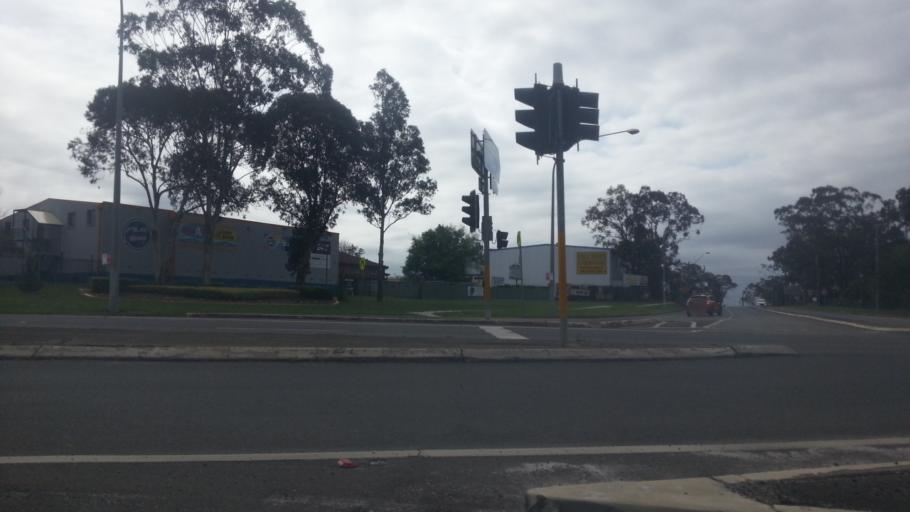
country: AU
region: New South Wales
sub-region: Camden
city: Camden South
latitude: -34.0738
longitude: 150.6964
